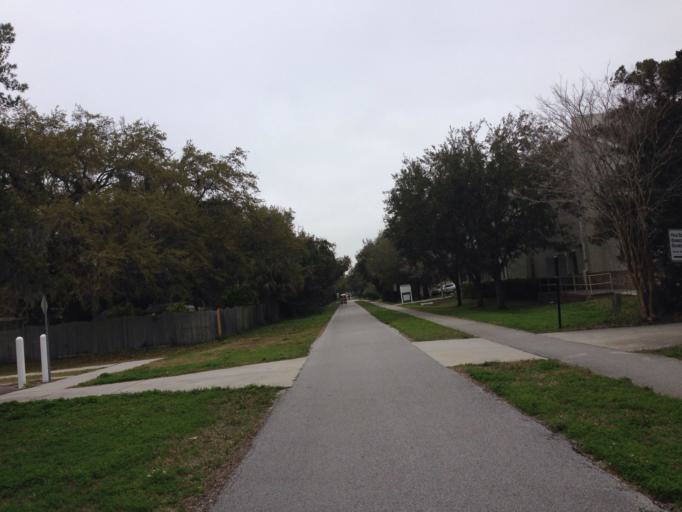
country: US
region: Florida
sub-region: Pinellas County
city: Dunedin
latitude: 28.0029
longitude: -82.7887
